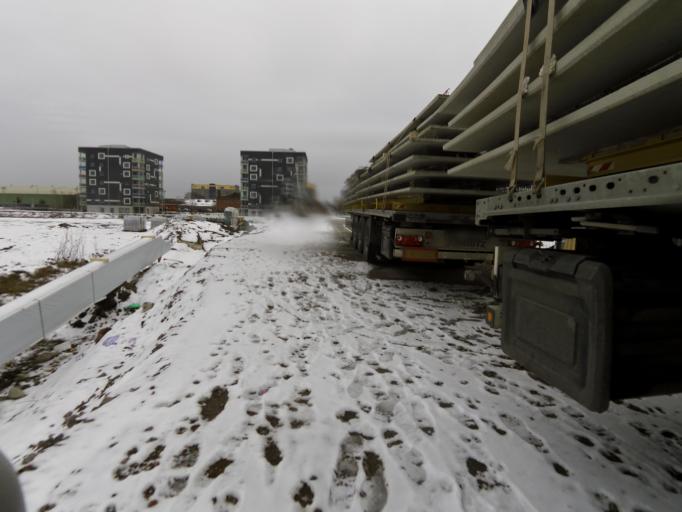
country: SE
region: Gaevleborg
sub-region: Gavle Kommun
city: Gavle
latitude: 60.6817
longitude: 17.1692
